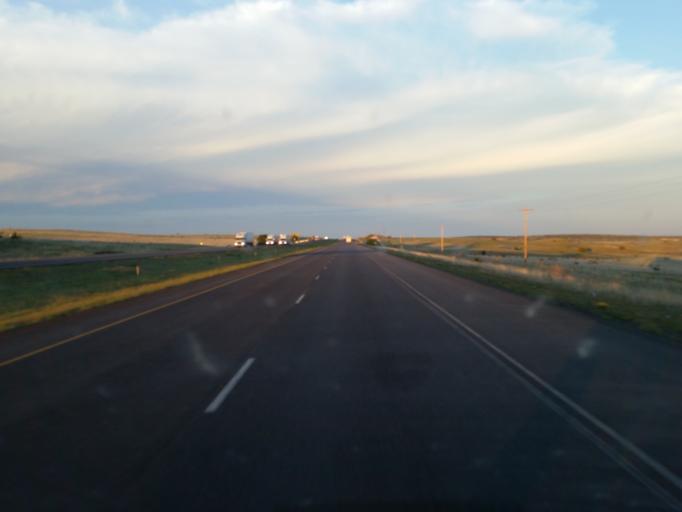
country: US
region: New Mexico
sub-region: Guadalupe County
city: Santa Rosa
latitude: 34.9908
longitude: -105.2827
